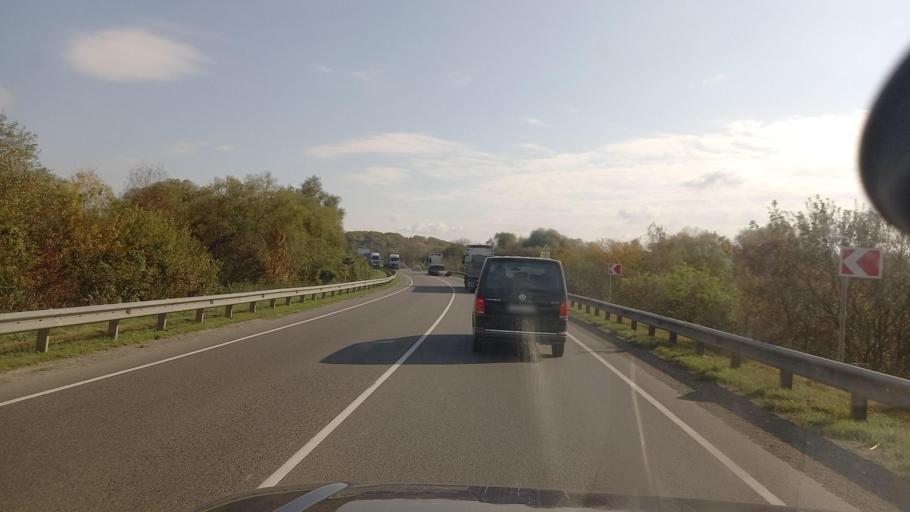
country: RU
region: Krasnodarskiy
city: Abinsk
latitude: 44.8406
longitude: 38.1637
